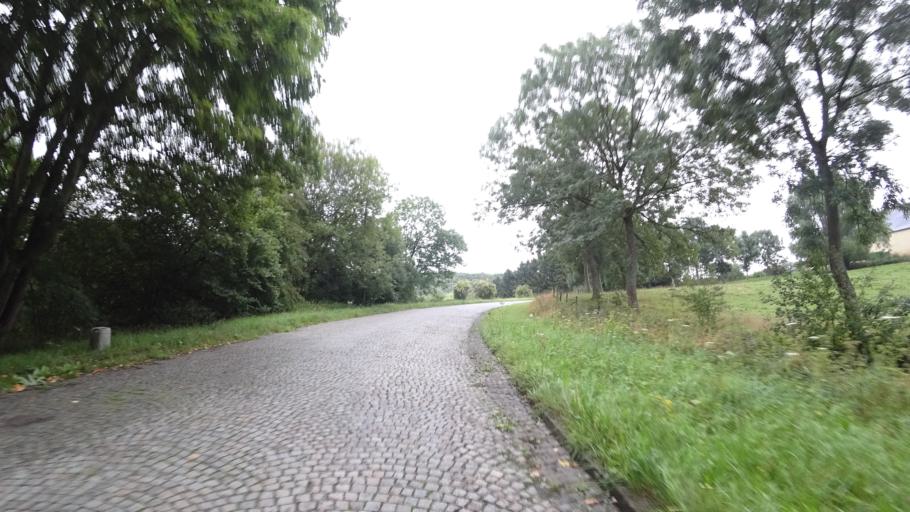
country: BE
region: Wallonia
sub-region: Province de Namur
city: Namur
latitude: 50.4882
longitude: 4.8272
